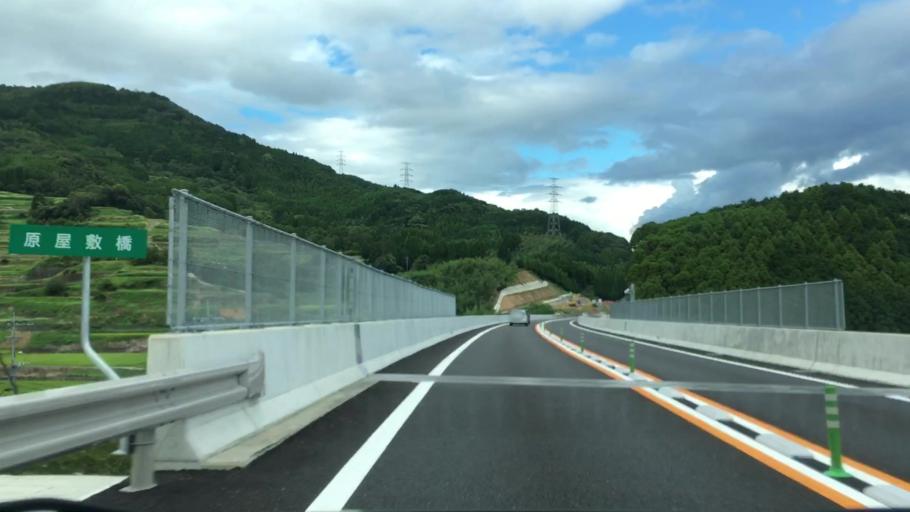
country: JP
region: Saga Prefecture
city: Imaricho-ko
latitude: 33.3108
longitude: 129.9172
